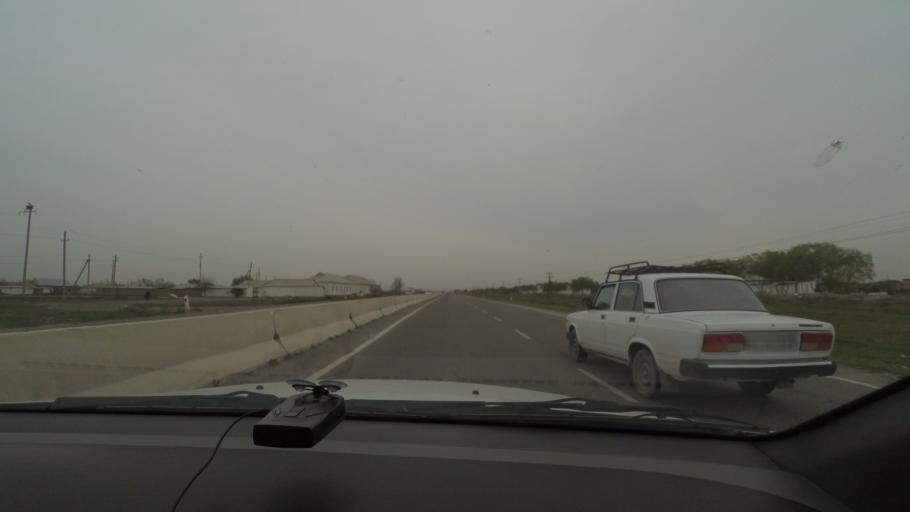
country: UZ
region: Sirdaryo
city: Guliston
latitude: 40.4961
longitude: 68.6256
